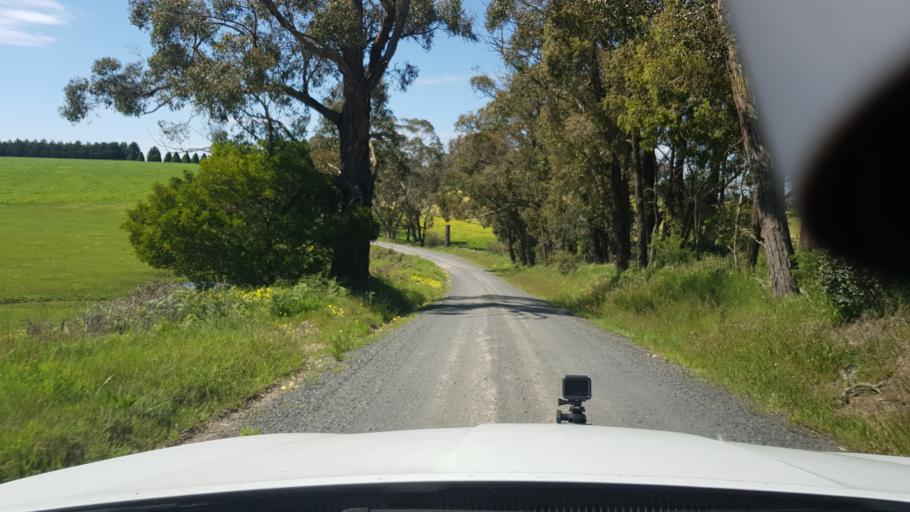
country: AU
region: Victoria
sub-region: Latrobe
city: Moe
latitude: -38.1338
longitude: 146.1098
